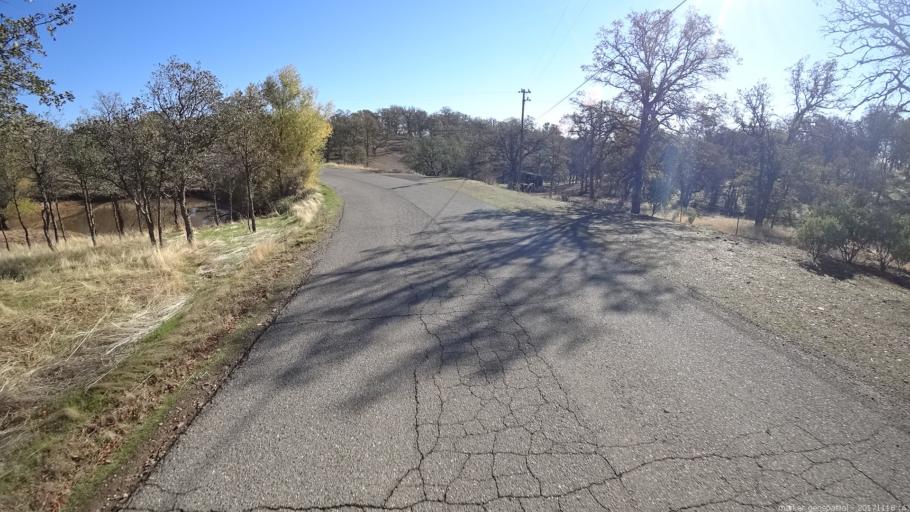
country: US
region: California
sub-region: Shasta County
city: Cottonwood
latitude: 40.3944
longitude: -122.3220
